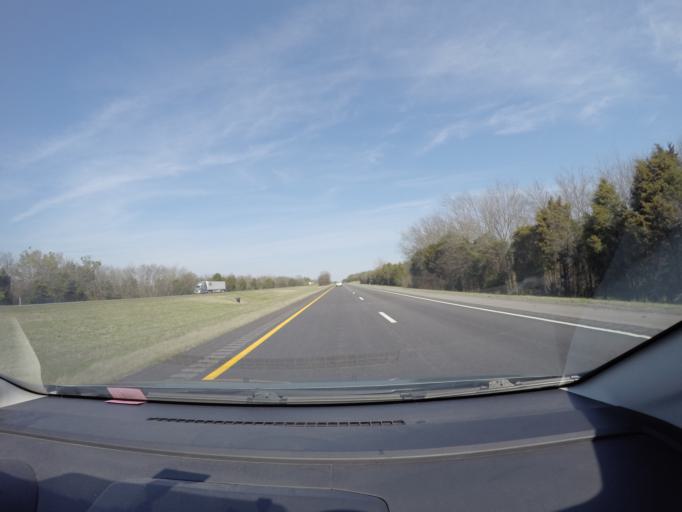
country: US
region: Tennessee
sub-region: Rutherford County
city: Plainview
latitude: 35.6875
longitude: -86.2934
